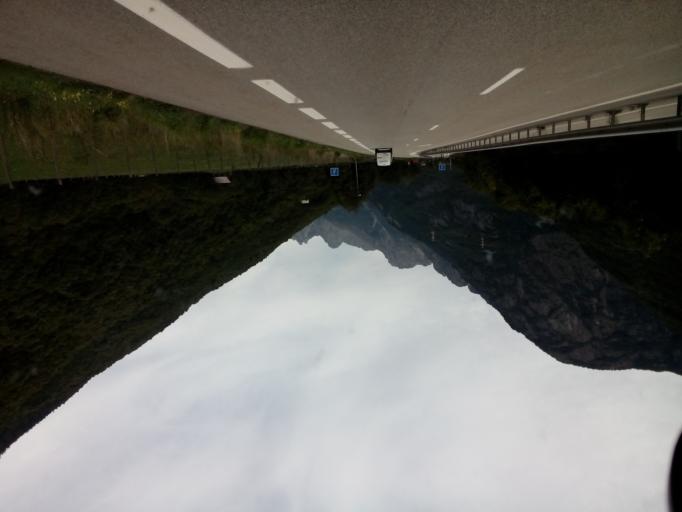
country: FR
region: Rhone-Alpes
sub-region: Departement de l'Isere
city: Vaulnaveys-le-Bas
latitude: 45.0614
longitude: 5.8650
